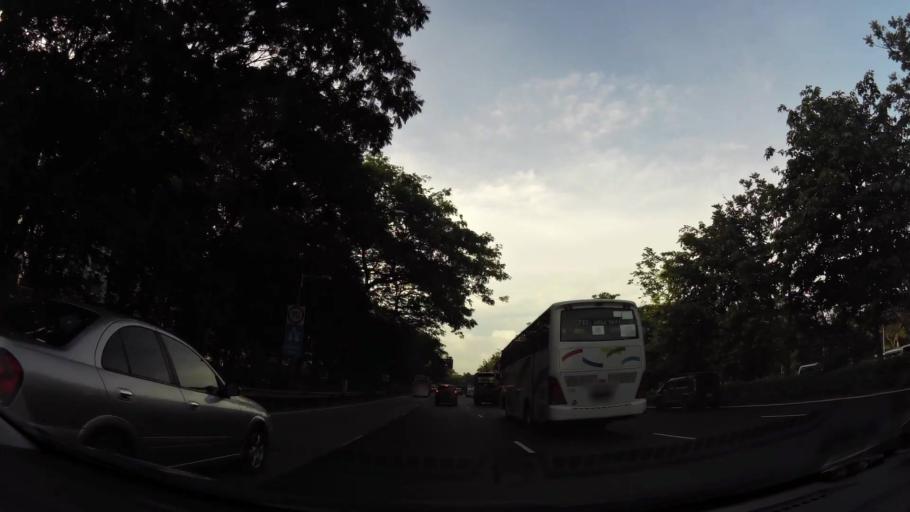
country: MY
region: Johor
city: Johor Bahru
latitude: 1.3511
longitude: 103.6951
